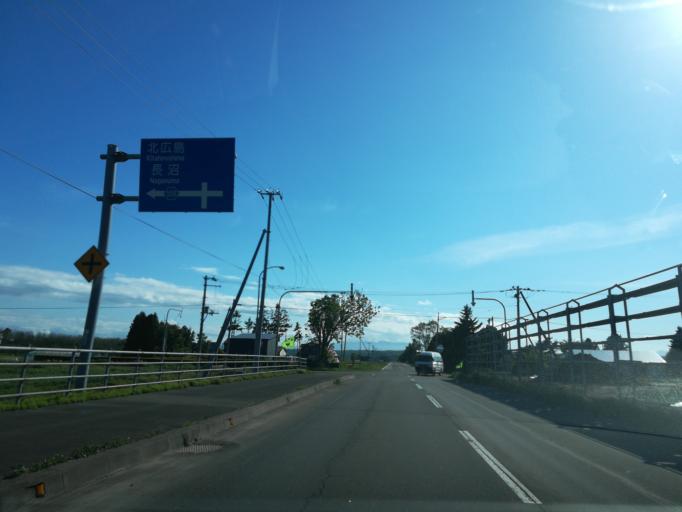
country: JP
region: Hokkaido
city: Kitahiroshima
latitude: 43.0409
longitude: 141.5849
